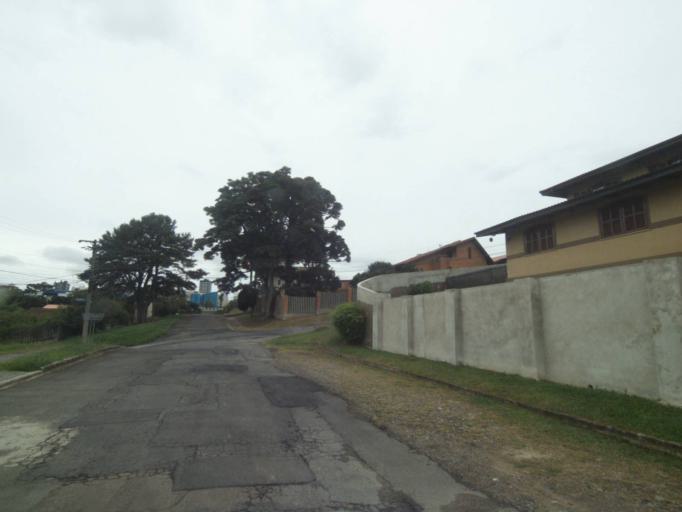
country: BR
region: Parana
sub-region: Curitiba
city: Curitiba
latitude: -25.4287
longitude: -49.3276
